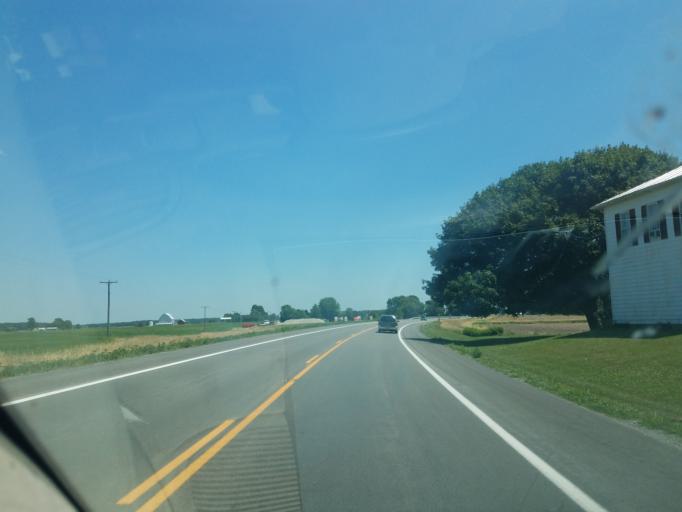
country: US
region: Ohio
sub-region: Hardin County
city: Ada
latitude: 40.7329
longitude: -83.7994
